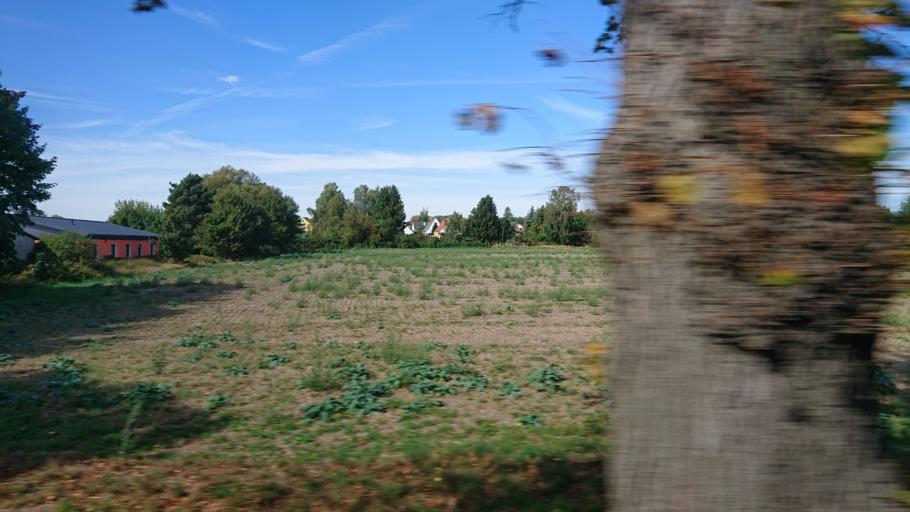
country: DE
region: Brandenburg
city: Bernau bei Berlin
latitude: 52.6381
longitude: 13.5588
